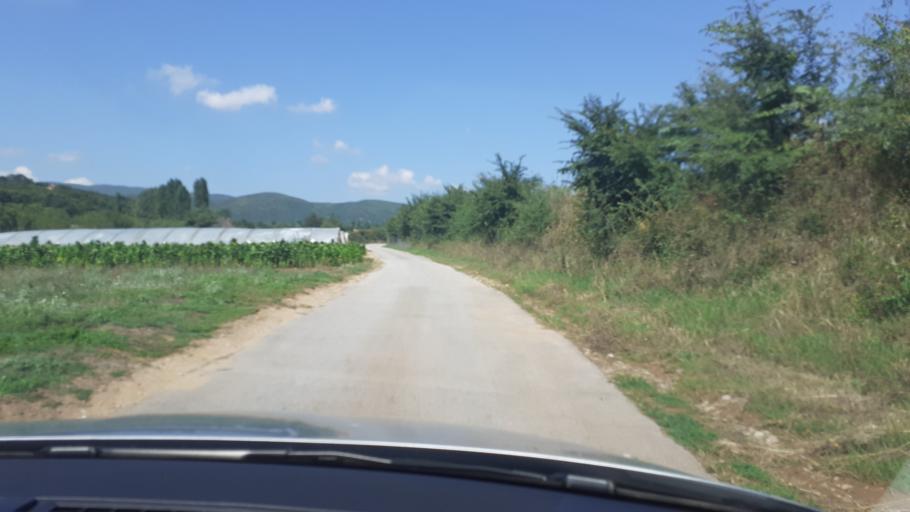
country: MK
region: Strumica
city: Veljusa
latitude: 41.5197
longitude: 22.5990
